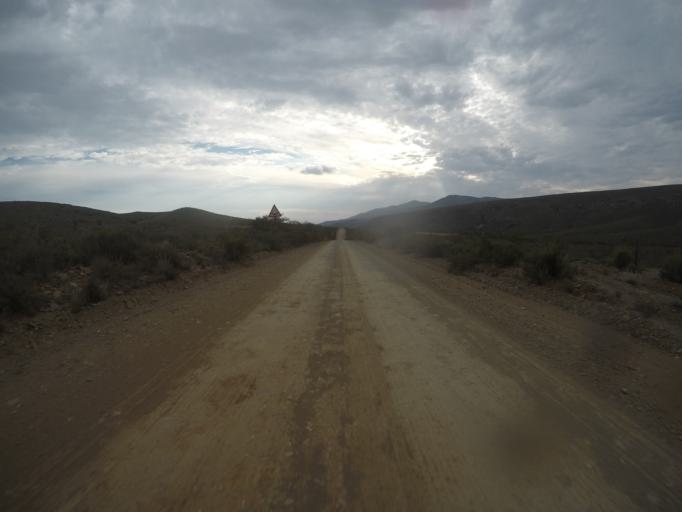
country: ZA
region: Eastern Cape
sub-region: Cacadu District Municipality
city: Willowmore
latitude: -33.4891
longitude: 23.5607
